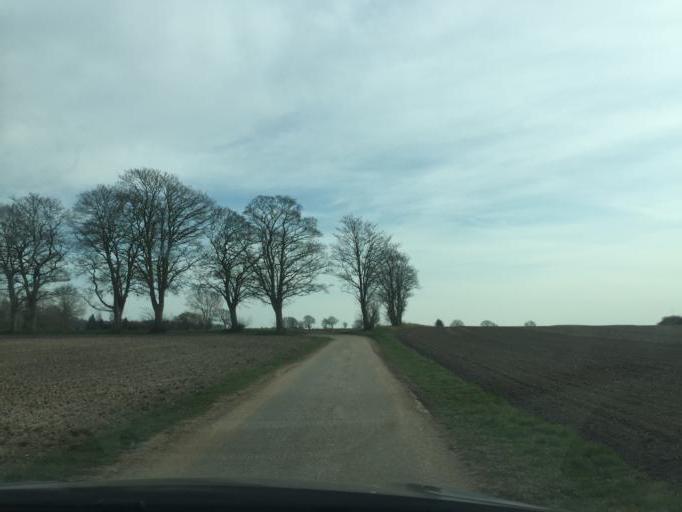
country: DK
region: South Denmark
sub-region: Faaborg-Midtfyn Kommune
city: Arslev
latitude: 55.3285
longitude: 10.5018
